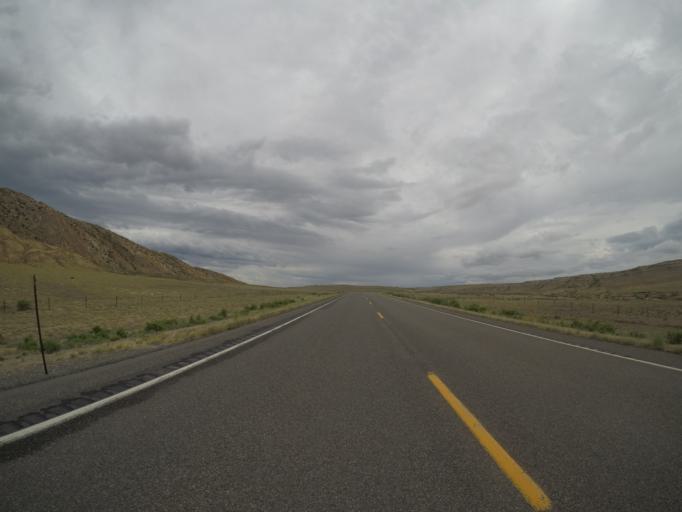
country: US
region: Wyoming
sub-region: Big Horn County
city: Lovell
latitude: 44.9416
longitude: -108.2964
